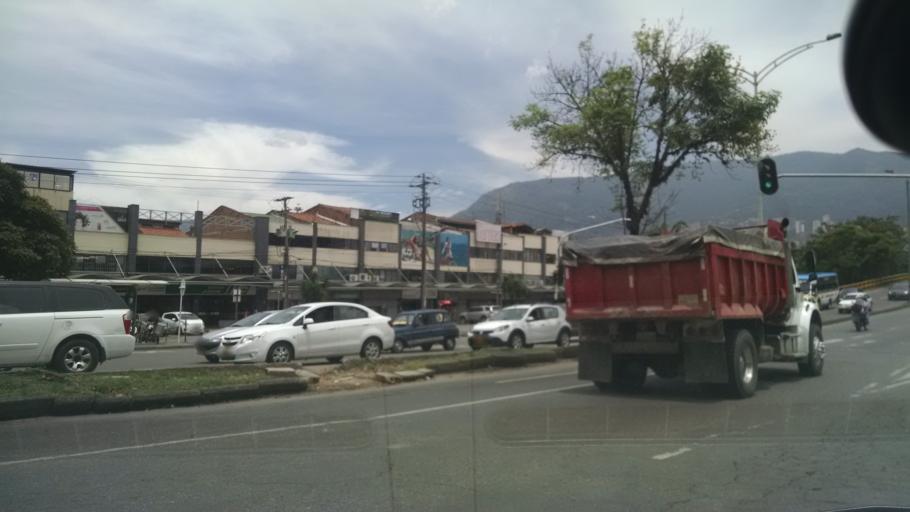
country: CO
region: Antioquia
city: Itagui
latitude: 6.2049
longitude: -75.5884
